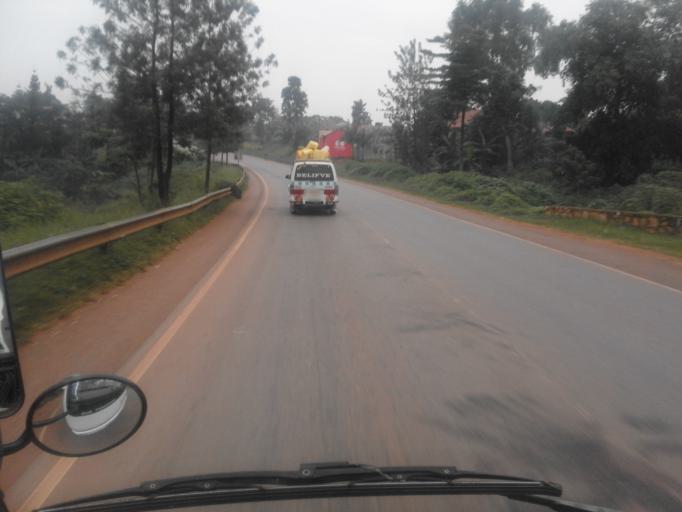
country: UG
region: Central Region
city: Lugazi
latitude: 0.3662
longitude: 32.9314
